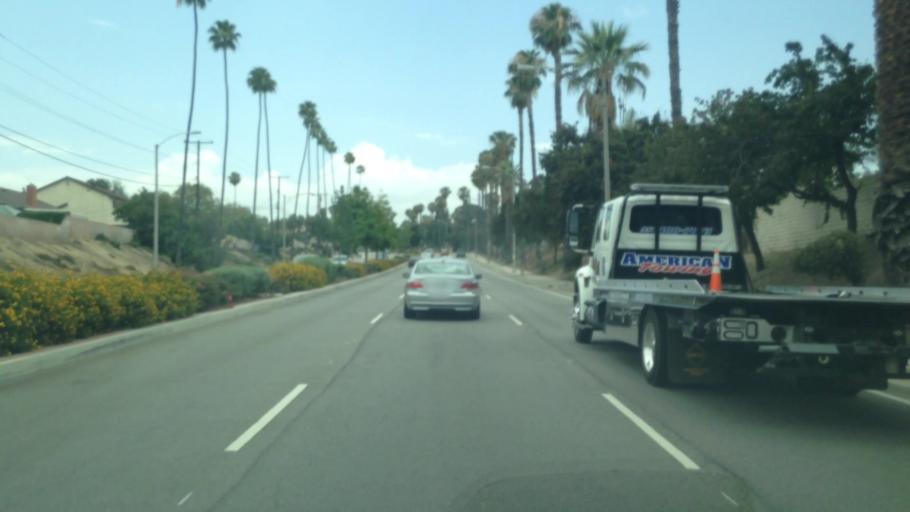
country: US
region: California
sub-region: Riverside County
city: Riverside
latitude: 33.9409
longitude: -117.3525
